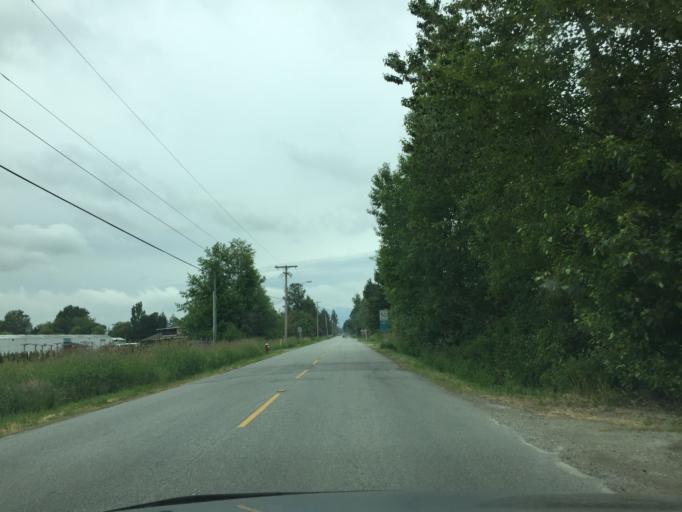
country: CA
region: British Columbia
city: Ladner
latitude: 49.1473
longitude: -123.0807
